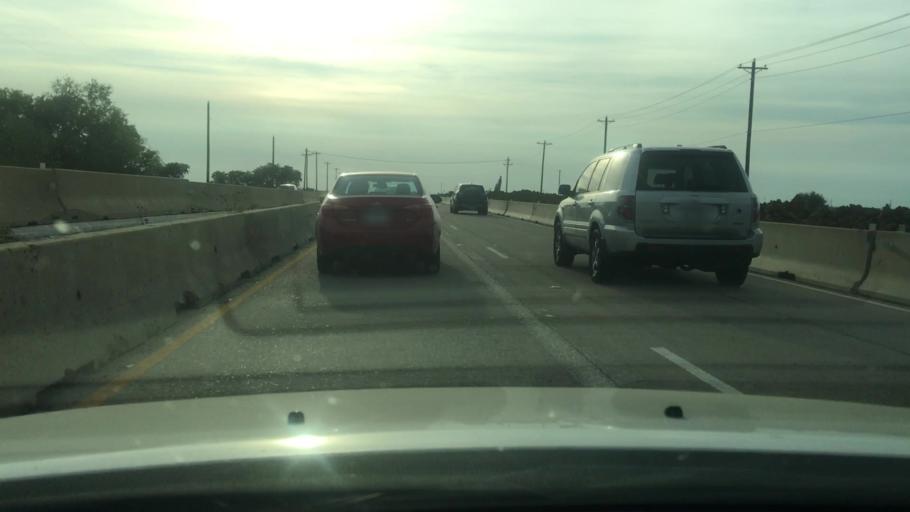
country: US
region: Texas
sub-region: Collin County
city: Prosper
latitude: 33.2193
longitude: -96.8364
